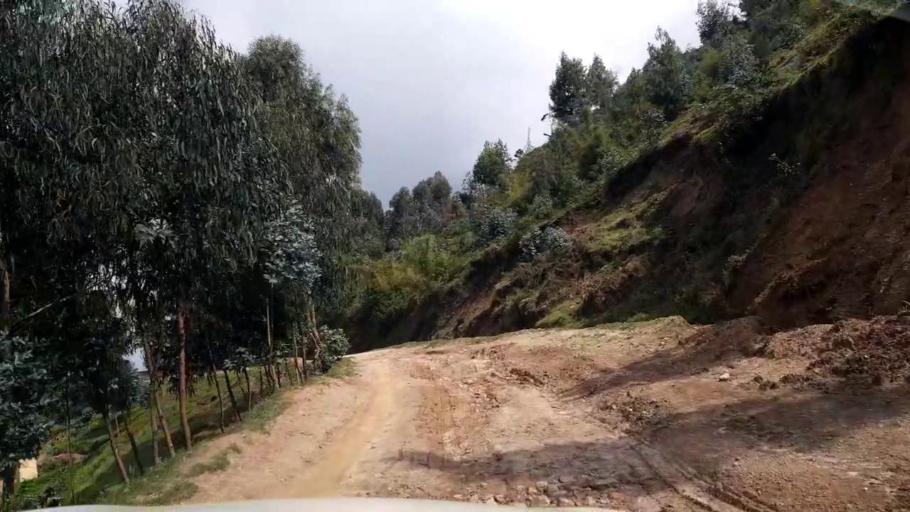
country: RW
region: Western Province
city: Kibuye
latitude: -1.8809
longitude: 29.4772
